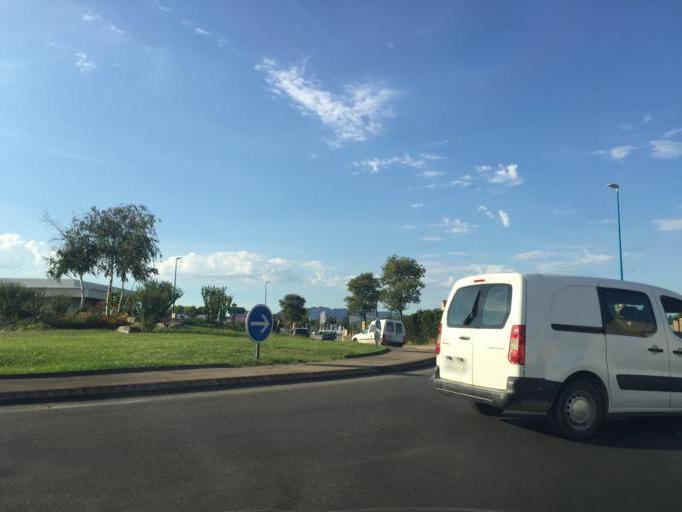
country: FR
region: Provence-Alpes-Cote d'Azur
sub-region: Departement du Vaucluse
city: Carpentras
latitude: 44.0318
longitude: 5.0519
